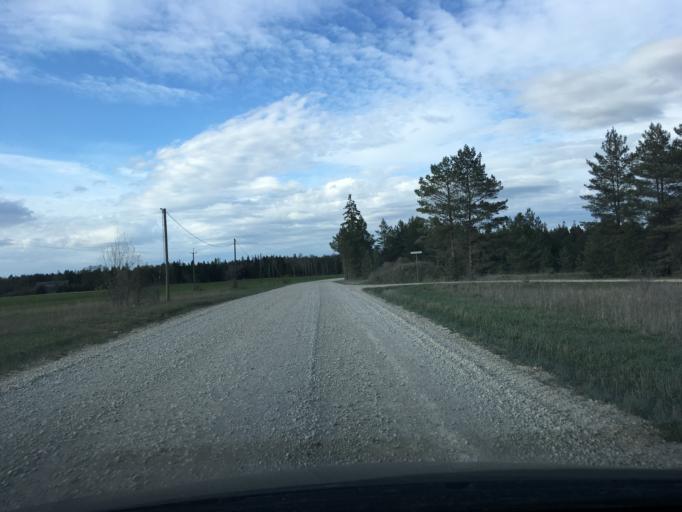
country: EE
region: Raplamaa
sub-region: Maerjamaa vald
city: Marjamaa
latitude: 58.9471
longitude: 24.3191
